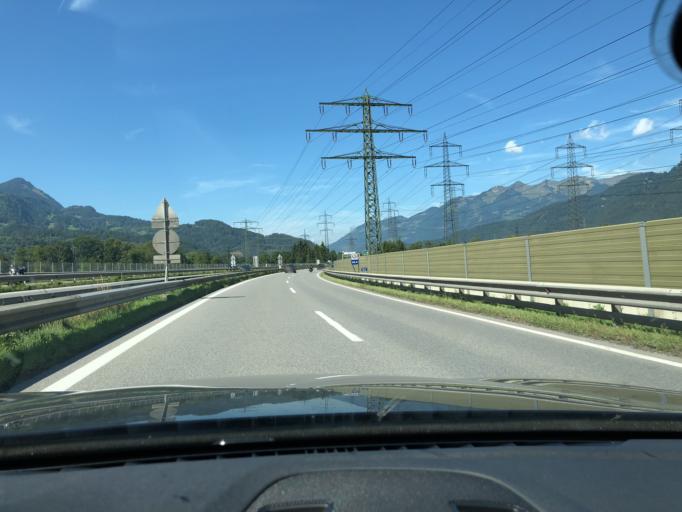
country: AT
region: Vorarlberg
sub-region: Politischer Bezirk Bludenz
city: Bludenz
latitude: 47.1384
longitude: 9.8281
